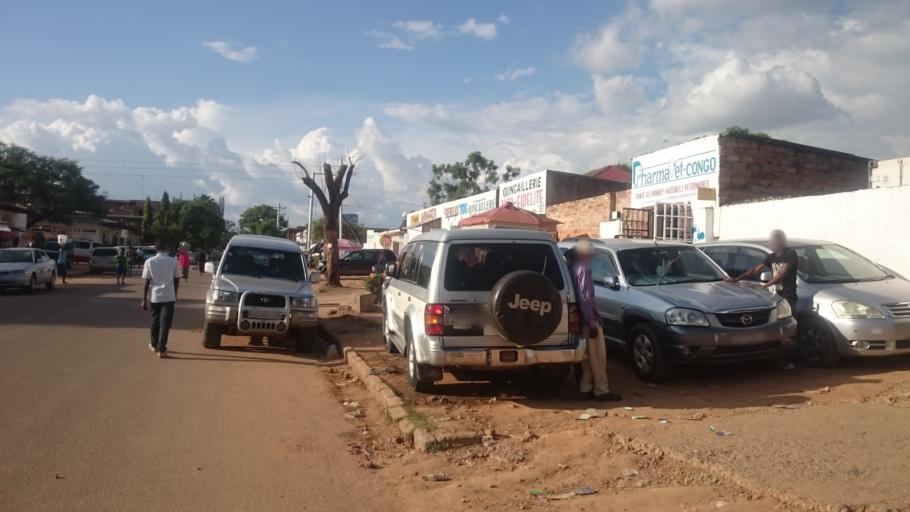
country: CD
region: Katanga
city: Lubumbashi
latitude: -11.6724
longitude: 27.4841
